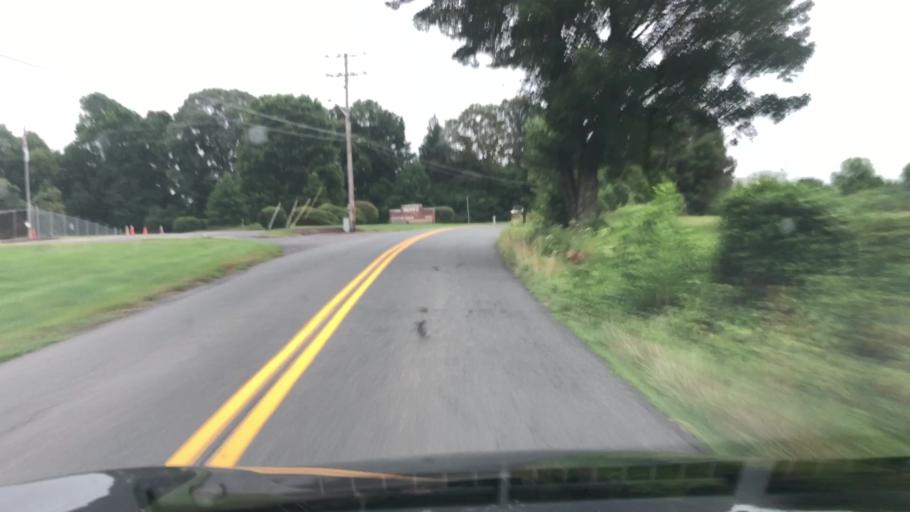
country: US
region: Virginia
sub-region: Stafford County
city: Stafford
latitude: 38.4905
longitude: -77.5866
